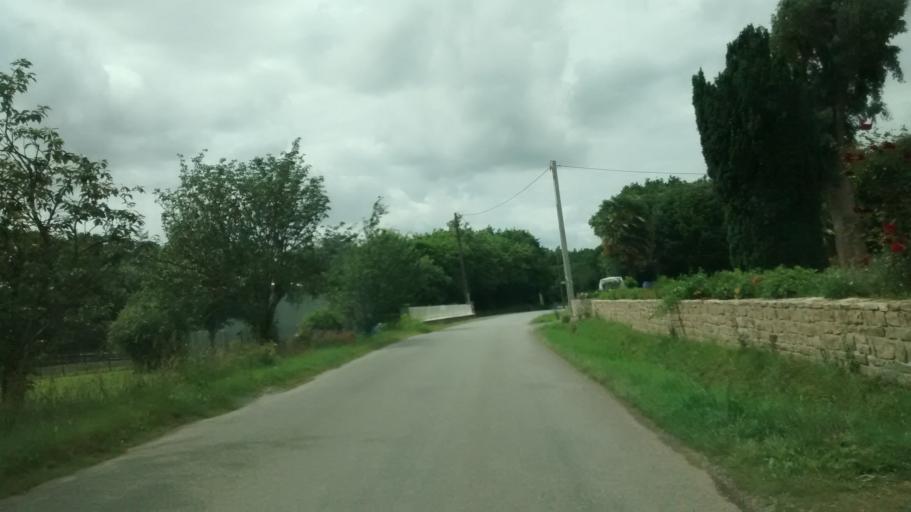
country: FR
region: Brittany
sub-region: Departement du Morbihan
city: Carentoir
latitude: 47.8243
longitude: -2.1624
